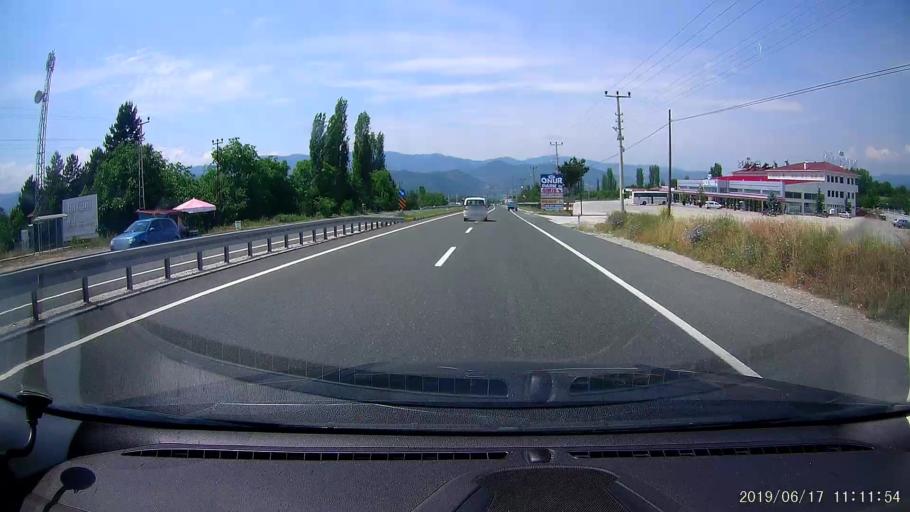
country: TR
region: Kastamonu
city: Tosya
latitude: 40.9801
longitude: 34.0032
